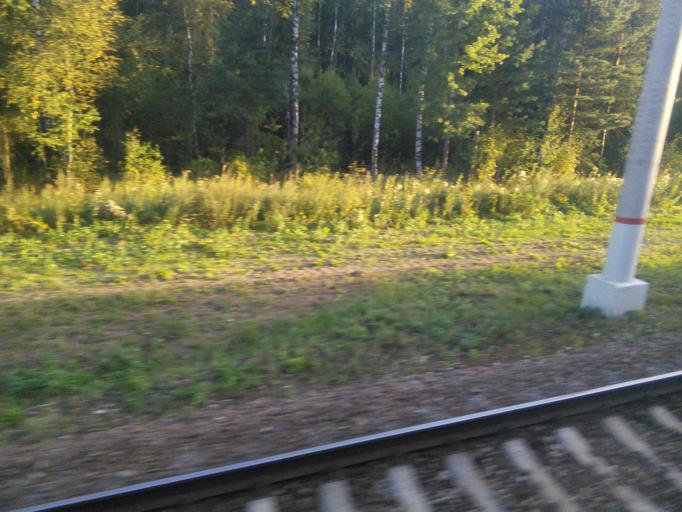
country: RU
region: Moskovskaya
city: Fryazevo
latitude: 55.7199
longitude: 38.4005
